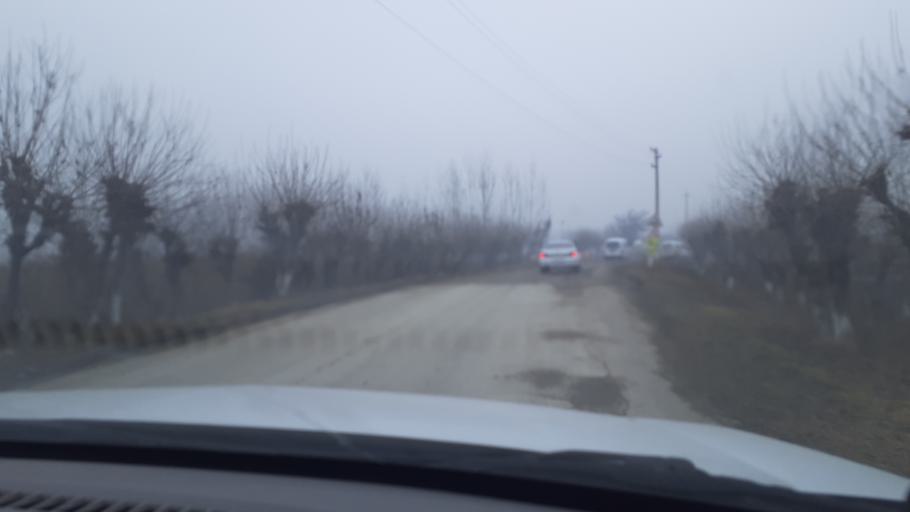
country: UZ
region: Namangan
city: Haqqulobod
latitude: 40.9010
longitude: 71.9968
